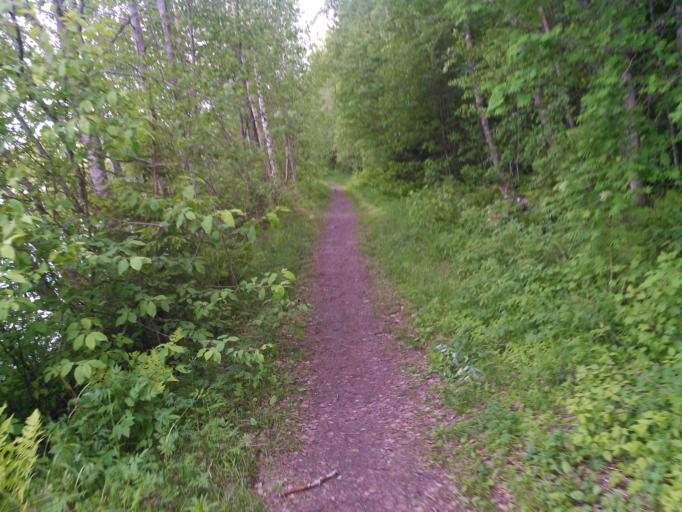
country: SE
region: Vaesterbotten
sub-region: Umea Kommun
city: Roback
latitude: 63.8235
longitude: 20.2055
